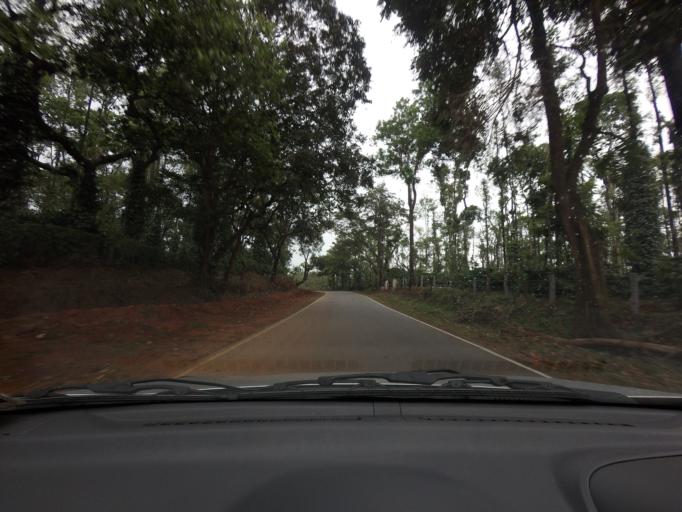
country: IN
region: Karnataka
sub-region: Hassan
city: Sakleshpur
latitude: 12.9445
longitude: 75.7520
